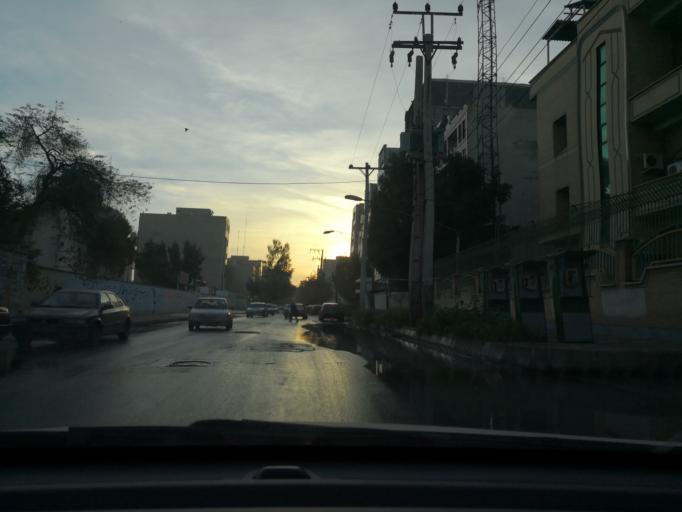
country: IR
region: Khuzestan
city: Ahvaz
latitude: 31.3519
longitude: 48.6807
